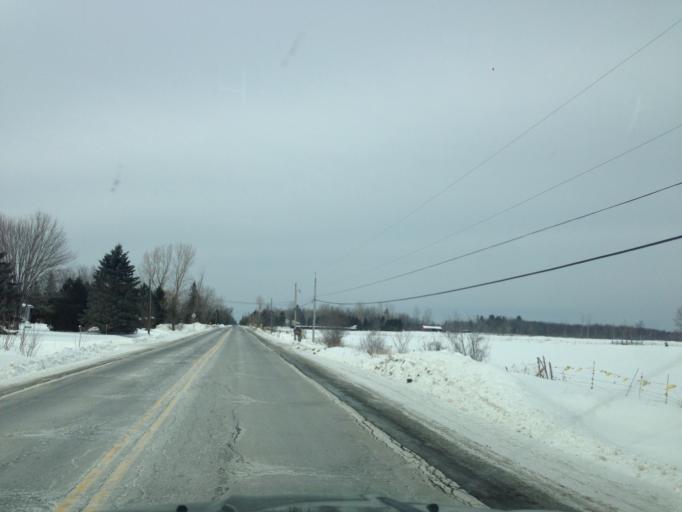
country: CA
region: Ontario
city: Ottawa
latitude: 45.3176
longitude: -75.5376
